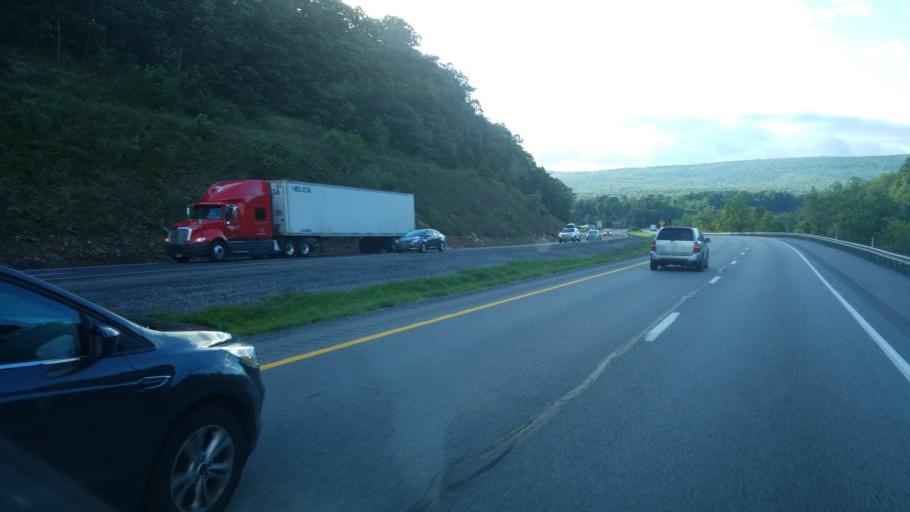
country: US
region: Pennsylvania
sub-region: Bedford County
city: Earlston
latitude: 39.9511
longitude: -78.2364
